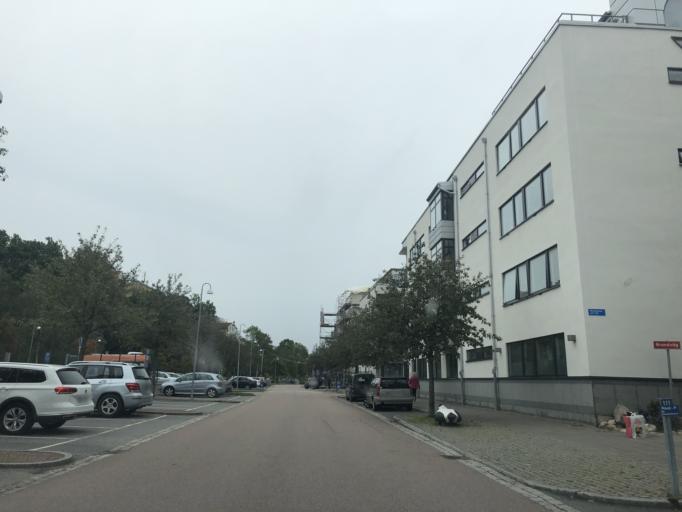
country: SE
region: Vaestra Goetaland
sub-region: Goteborg
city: Majorna
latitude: 57.7061
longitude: 11.9286
